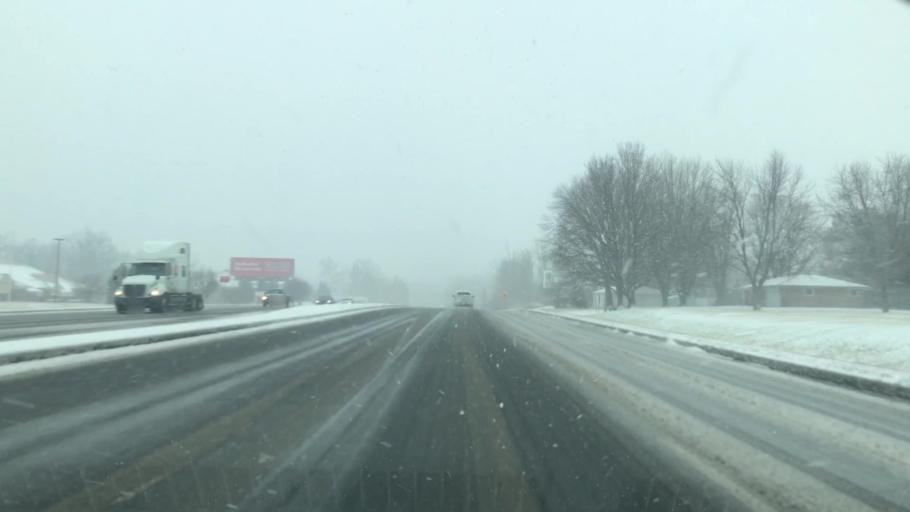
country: US
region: Indiana
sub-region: Marion County
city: Southport
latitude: 39.6755
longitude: -86.1493
